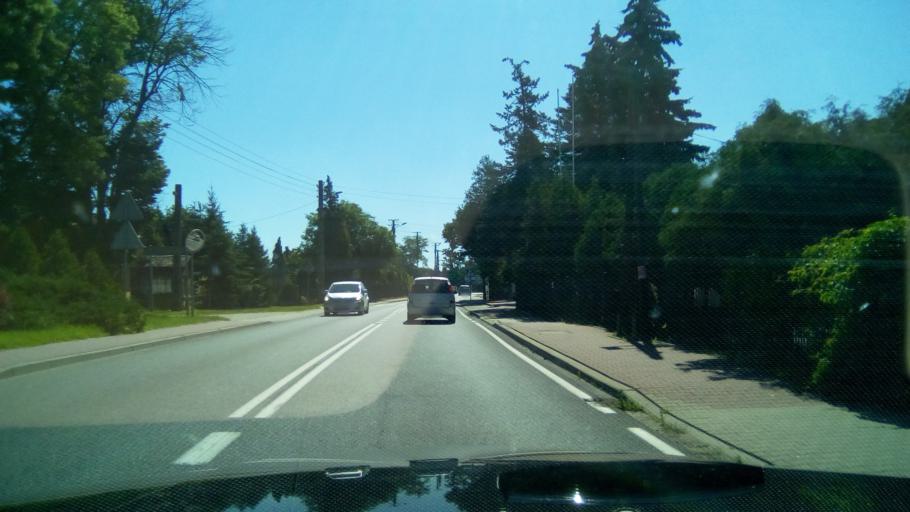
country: PL
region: Lodz Voivodeship
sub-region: Powiat tomaszowski
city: Inowlodz
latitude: 51.5262
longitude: 20.2213
